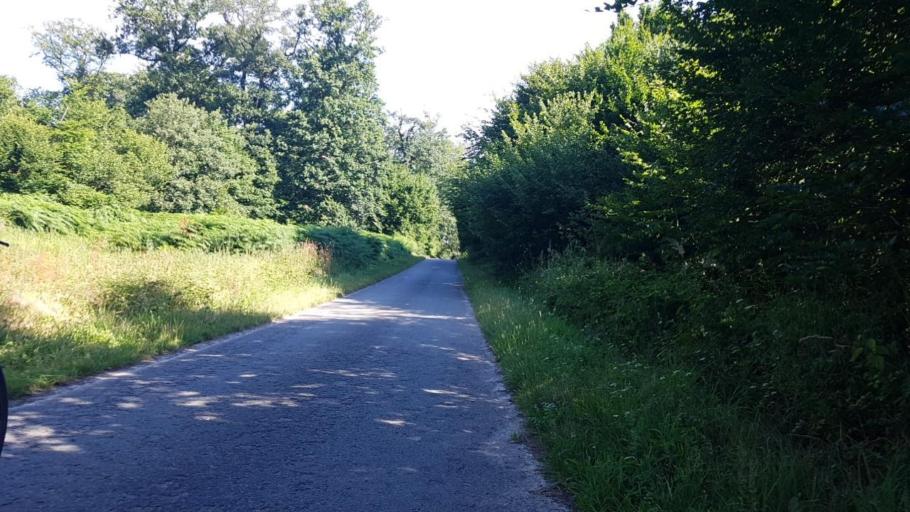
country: FR
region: Picardie
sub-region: Departement de l'Oise
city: Fleurines
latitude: 49.2616
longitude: 2.6190
